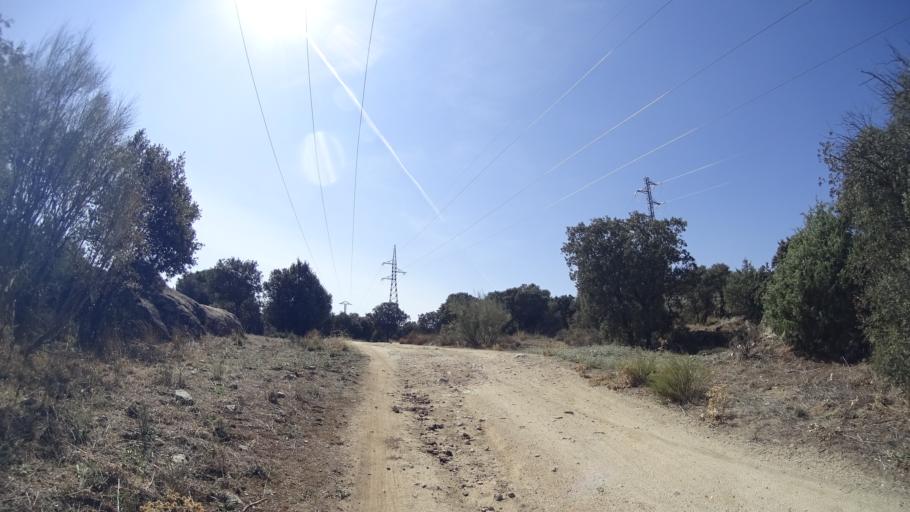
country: ES
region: Madrid
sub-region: Provincia de Madrid
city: Colmenarejo
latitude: 40.5759
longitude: -4.0259
